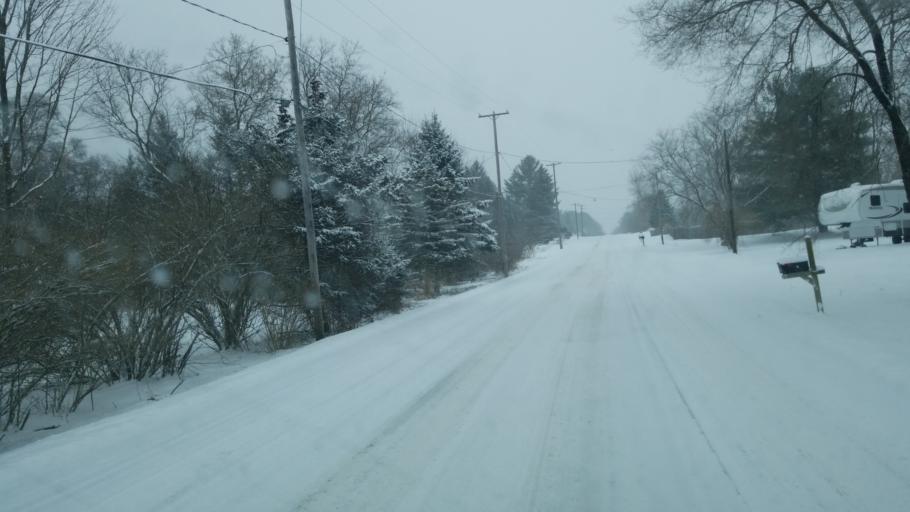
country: US
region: Michigan
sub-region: Mecosta County
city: Big Rapids
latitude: 43.5768
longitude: -85.4463
